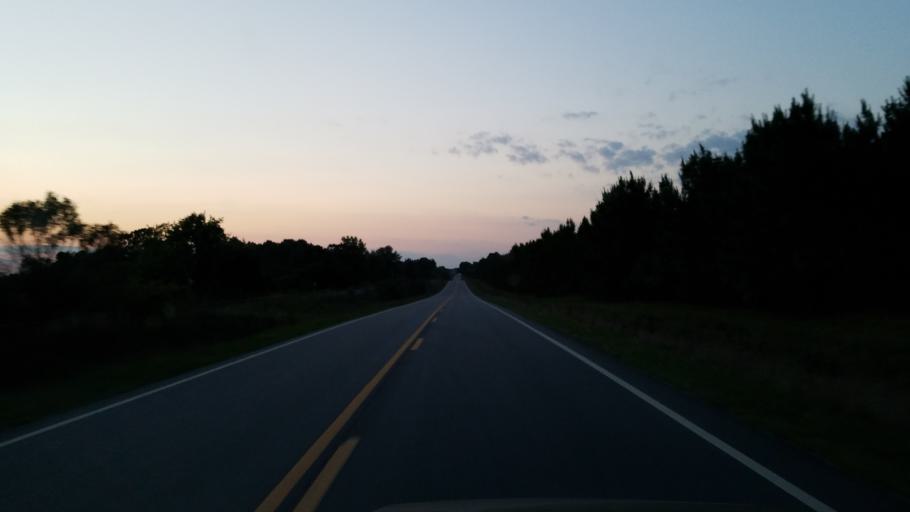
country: US
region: Georgia
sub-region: Turner County
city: Ashburn
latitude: 31.6243
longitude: -83.6090
